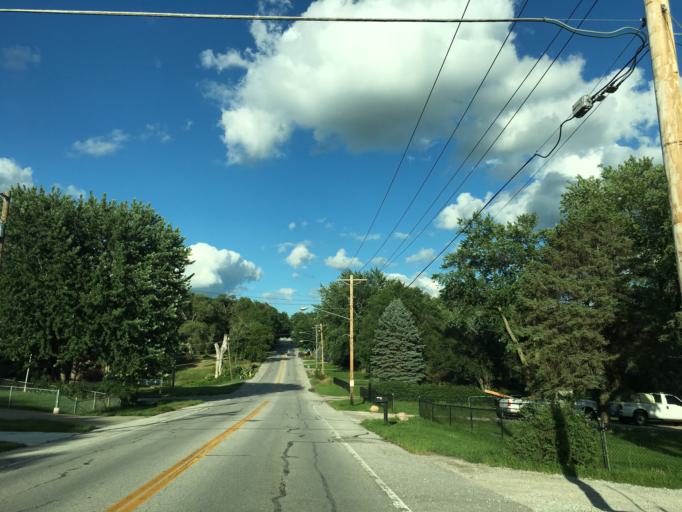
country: US
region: Nebraska
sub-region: Sarpy County
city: La Vista
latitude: 41.1836
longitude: -95.9630
